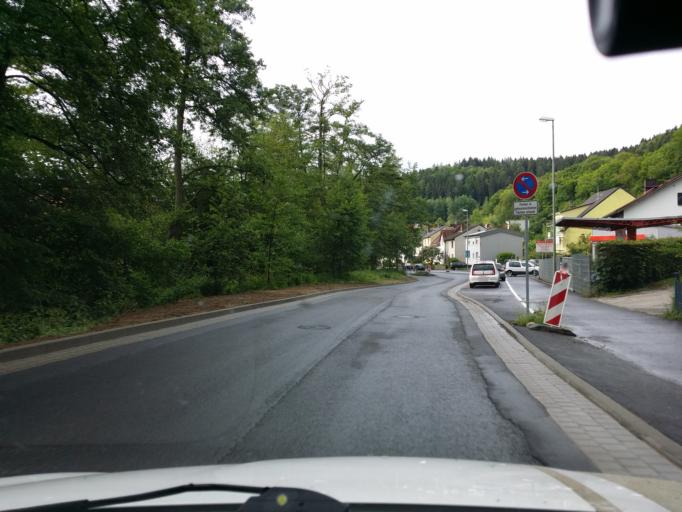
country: DE
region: Hesse
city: Eppstein
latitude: 50.1535
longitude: 8.3757
